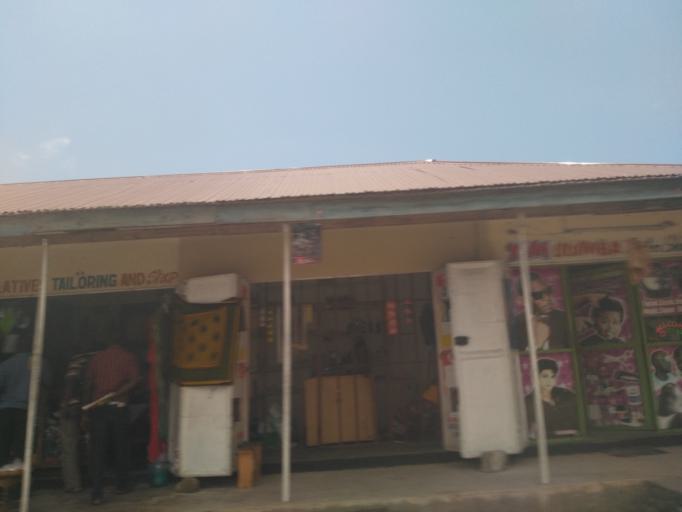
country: TZ
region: Dar es Salaam
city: Dar es Salaam
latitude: -6.8704
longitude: 39.2792
